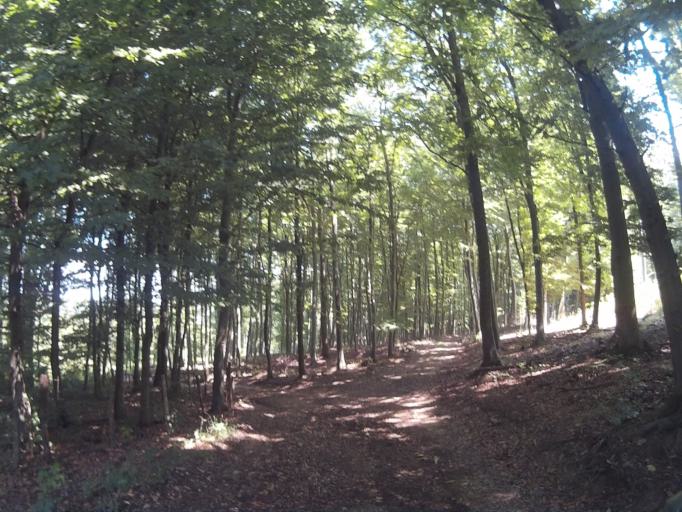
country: HU
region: Veszprem
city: Zirc
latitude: 47.2026
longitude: 17.8931
